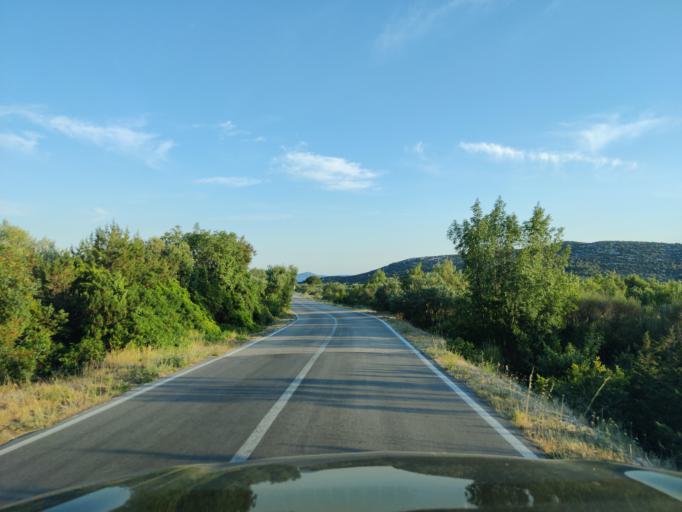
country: HR
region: Sibensko-Kniniska
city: Tribunj
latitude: 43.7802
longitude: 15.7280
